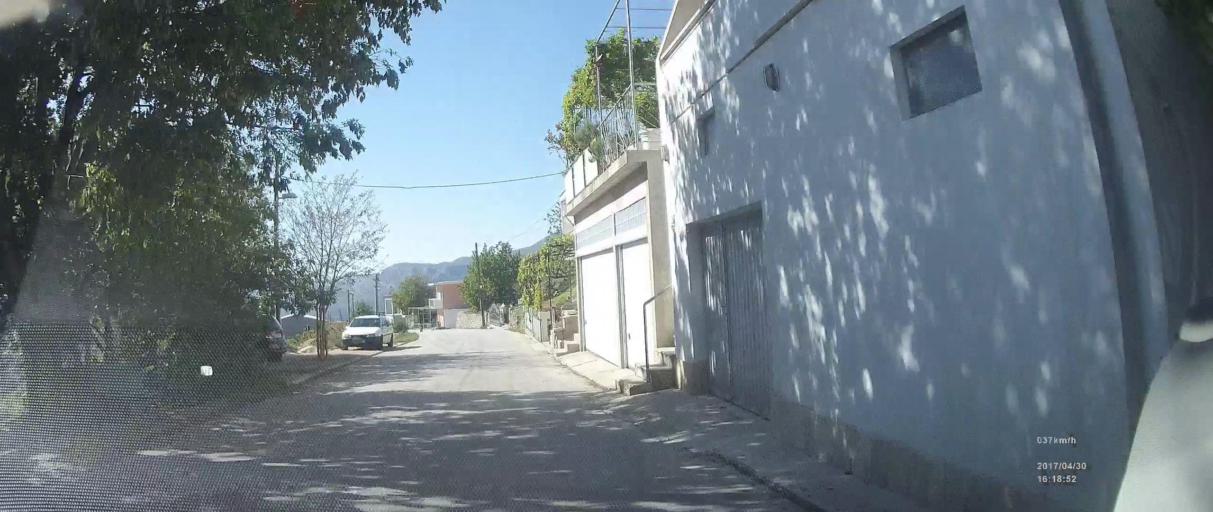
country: HR
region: Splitsko-Dalmatinska
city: Srinjine
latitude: 43.5004
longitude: 16.6048
